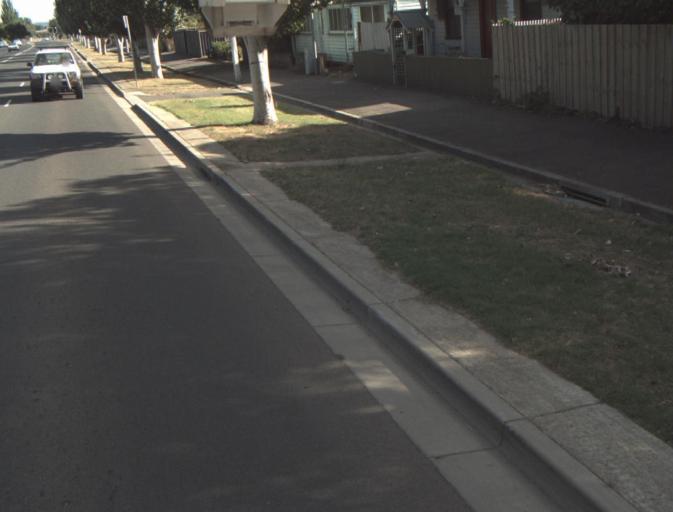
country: AU
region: Tasmania
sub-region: Launceston
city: Launceston
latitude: -41.4293
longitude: 147.1326
